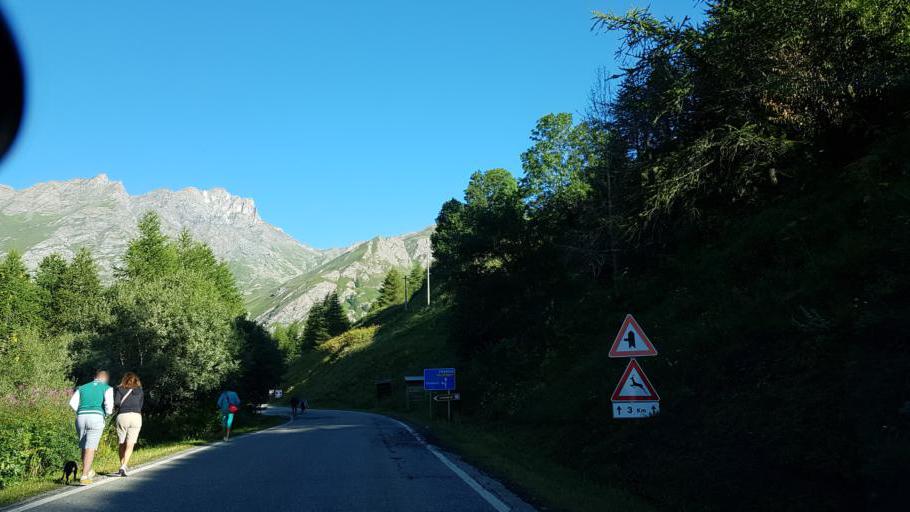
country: IT
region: Piedmont
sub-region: Provincia di Cuneo
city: Pontechianale
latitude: 44.6449
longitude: 7.0037
